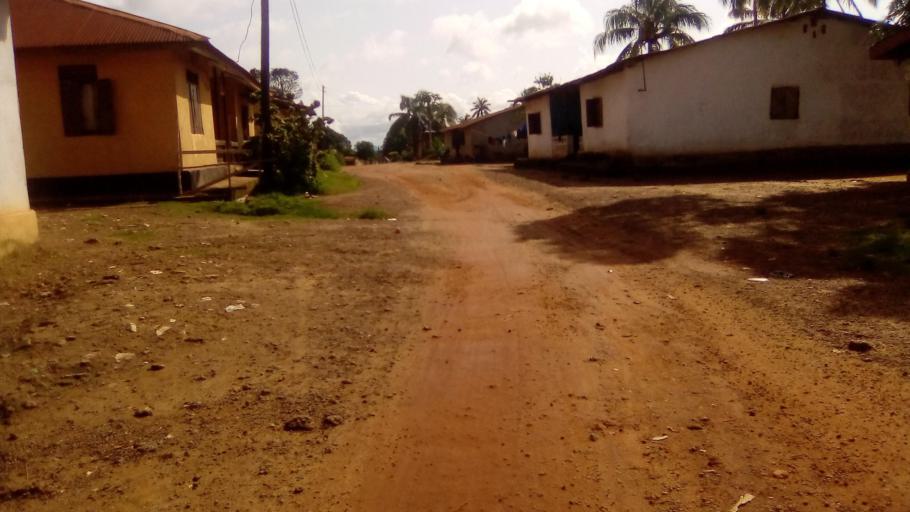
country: SL
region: Southern Province
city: Bo
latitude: 7.9719
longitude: -11.7320
